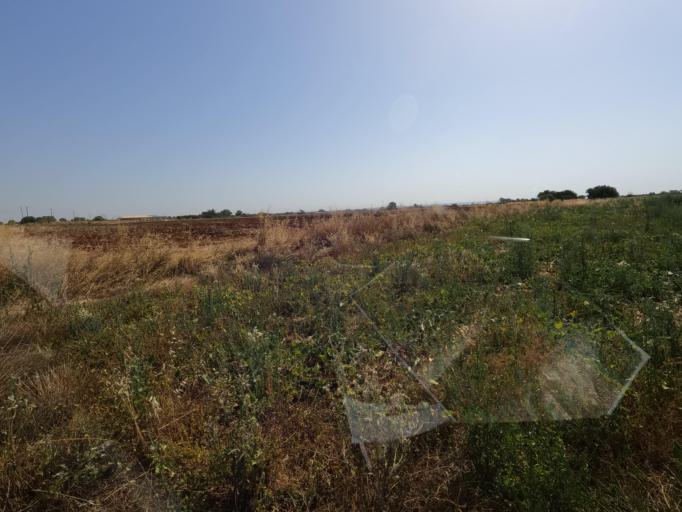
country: CY
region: Ammochostos
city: Liopetri
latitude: 34.9801
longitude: 33.8813
